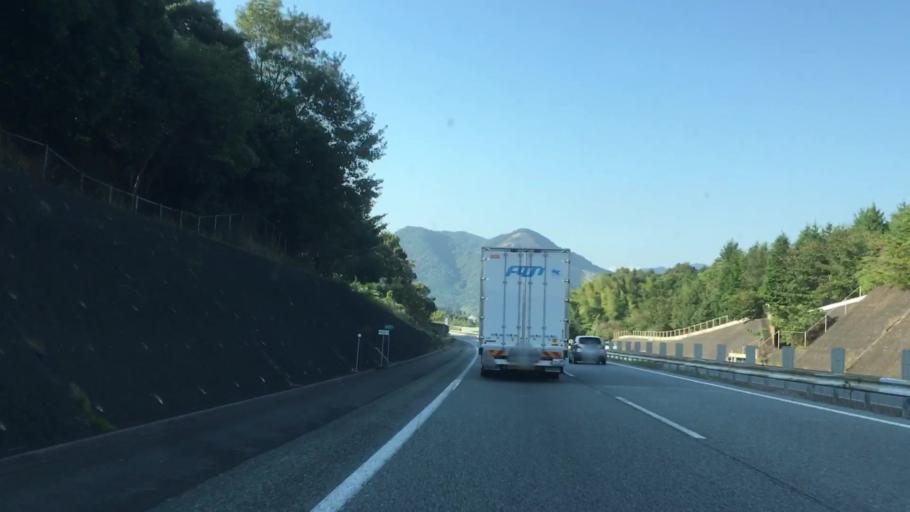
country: JP
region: Yamaguchi
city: Hofu
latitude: 34.0644
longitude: 131.5014
